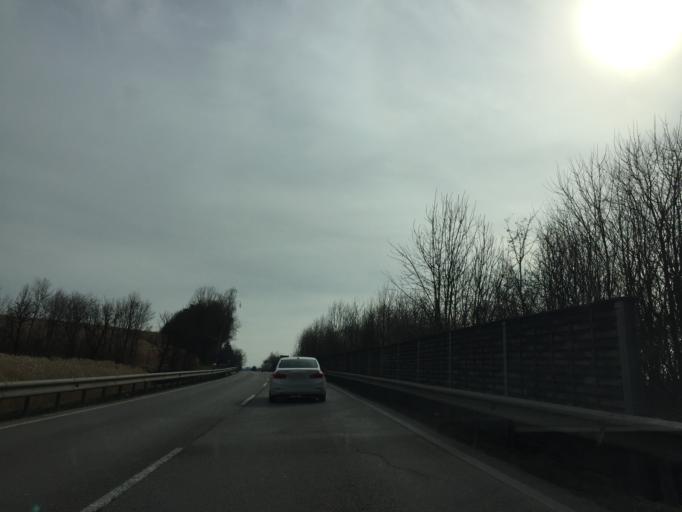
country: AT
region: Upper Austria
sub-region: Politischer Bezirk Ried im Innkreis
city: Ried im Innkreis
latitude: 48.2206
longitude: 13.4910
